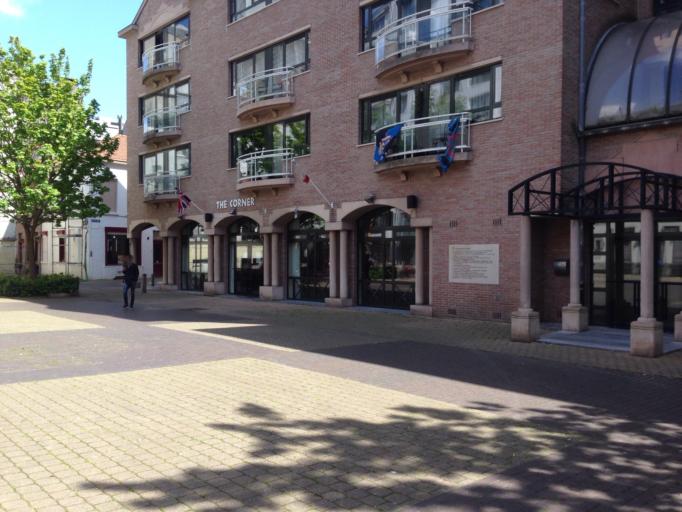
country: BE
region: Flanders
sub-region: Provincie West-Vlaanderen
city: Ostend
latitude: 51.2339
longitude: 2.9170
